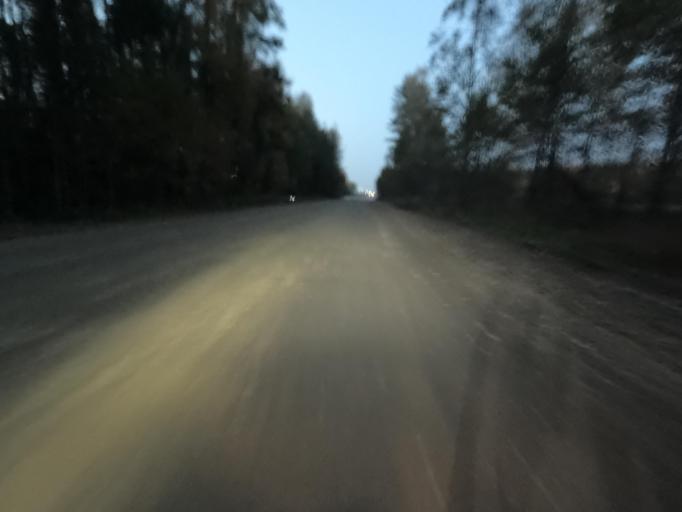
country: RU
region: Leningrad
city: Lyuban'
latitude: 59.1920
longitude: 31.2517
